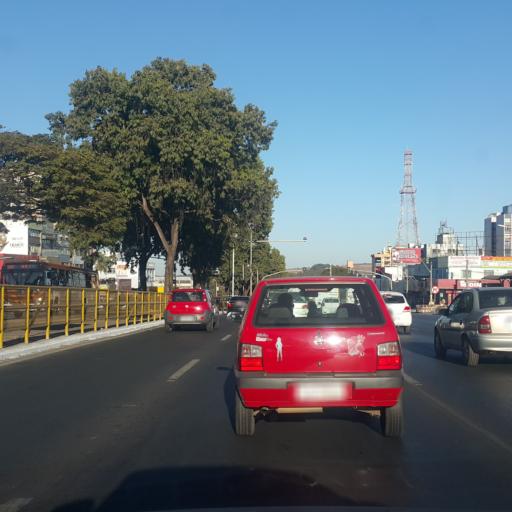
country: BR
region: Federal District
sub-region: Brasilia
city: Brasilia
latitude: -15.8334
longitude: -48.0562
